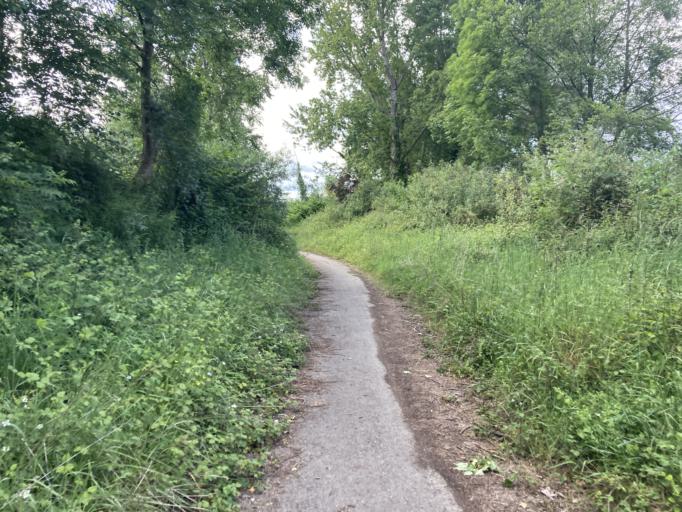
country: FR
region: Aquitaine
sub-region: Departement des Pyrenees-Atlantiques
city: Arbus
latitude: 43.3426
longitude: -0.5039
